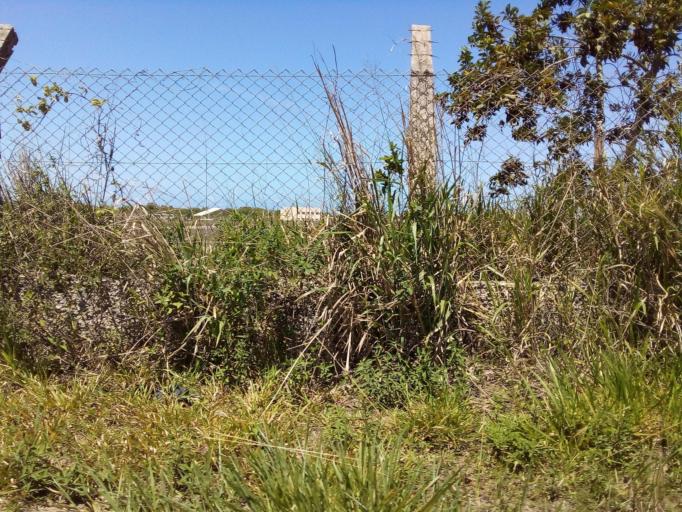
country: BR
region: Espirito Santo
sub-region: Aracruz
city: Aracruz
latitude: -19.8183
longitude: -40.0673
